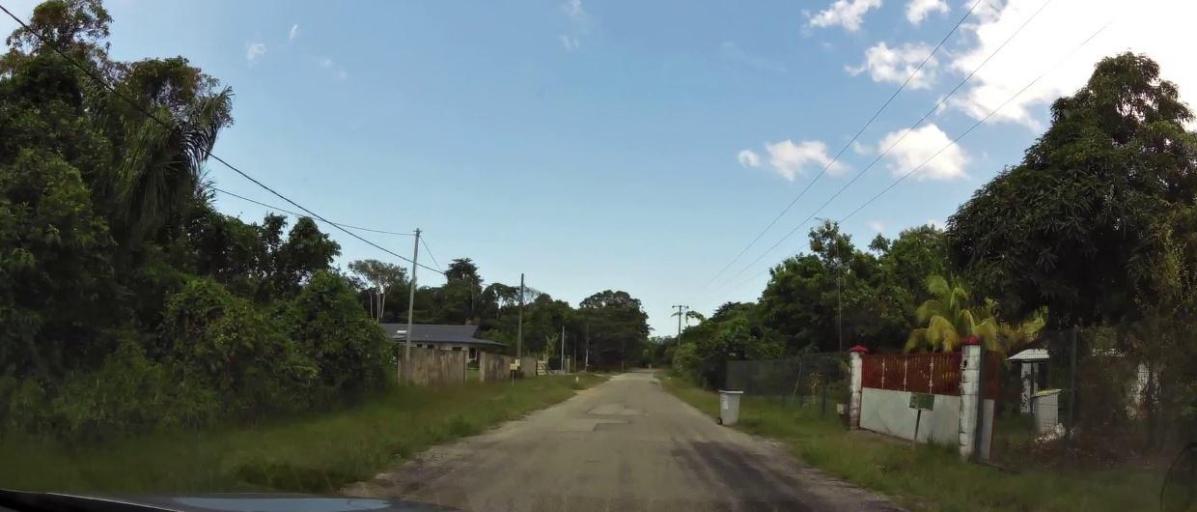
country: GF
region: Guyane
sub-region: Guyane
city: Matoury
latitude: 4.8327
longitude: -52.3064
